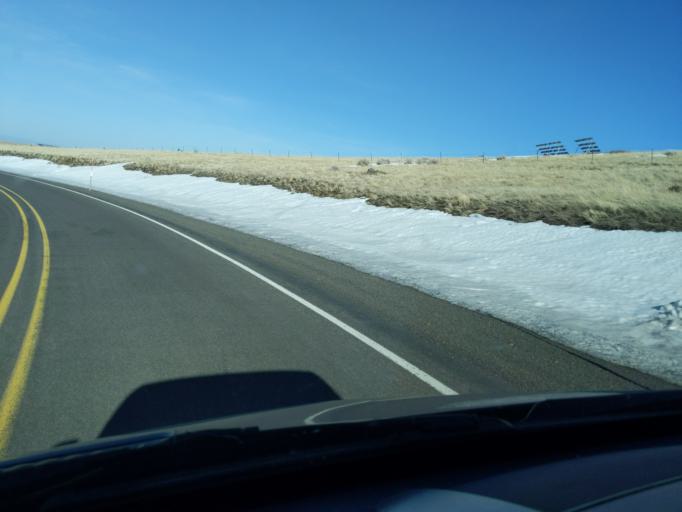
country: US
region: Oregon
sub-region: Umatilla County
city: Pilot Rock
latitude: 45.3021
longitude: -119.0052
